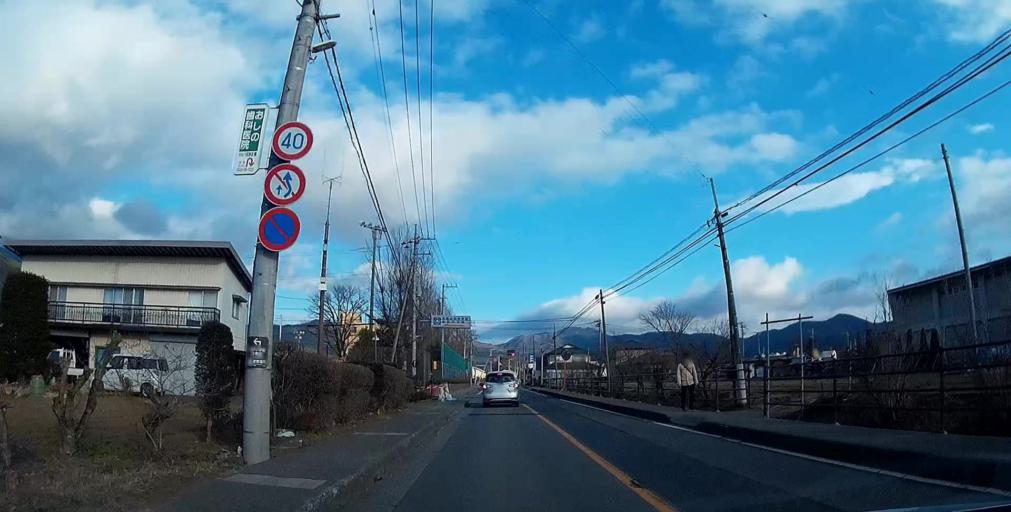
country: JP
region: Yamanashi
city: Fujikawaguchiko
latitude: 35.4598
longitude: 138.8461
